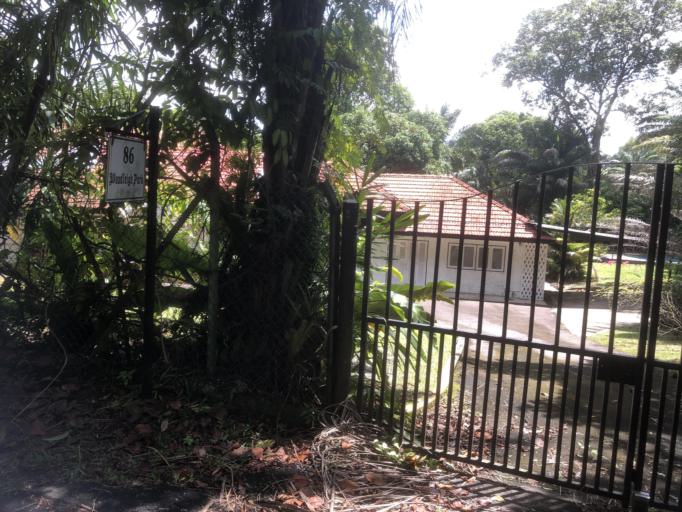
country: SG
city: Singapore
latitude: 1.3413
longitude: 103.8660
